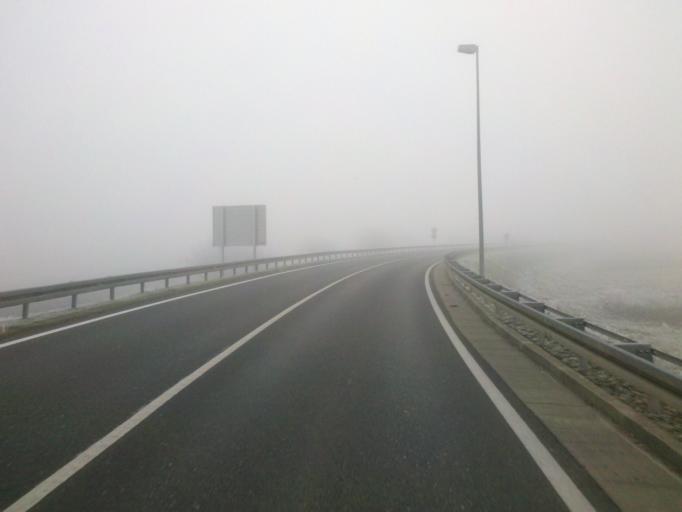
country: HR
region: Varazdinska
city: Jalkovec
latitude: 46.2915
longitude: 16.3085
